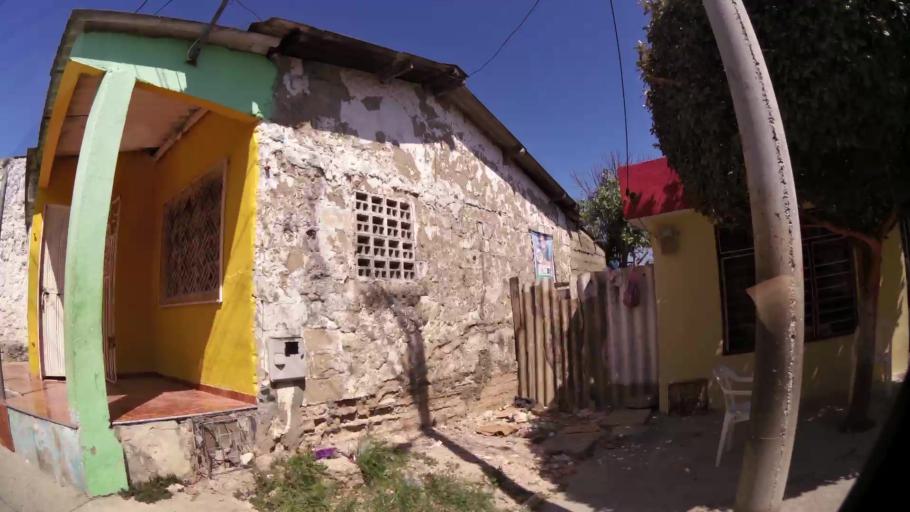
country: CO
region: Bolivar
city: Cartagena
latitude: 10.4303
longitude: -75.5176
